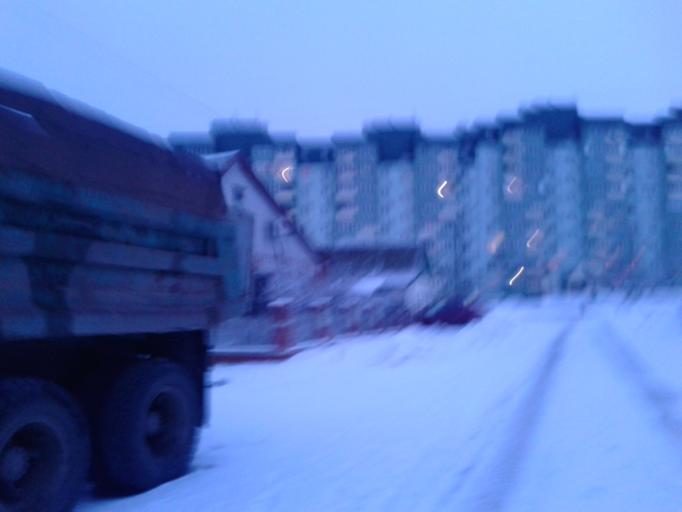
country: RU
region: Volgograd
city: Volgograd
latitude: 48.7599
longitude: 44.4890
